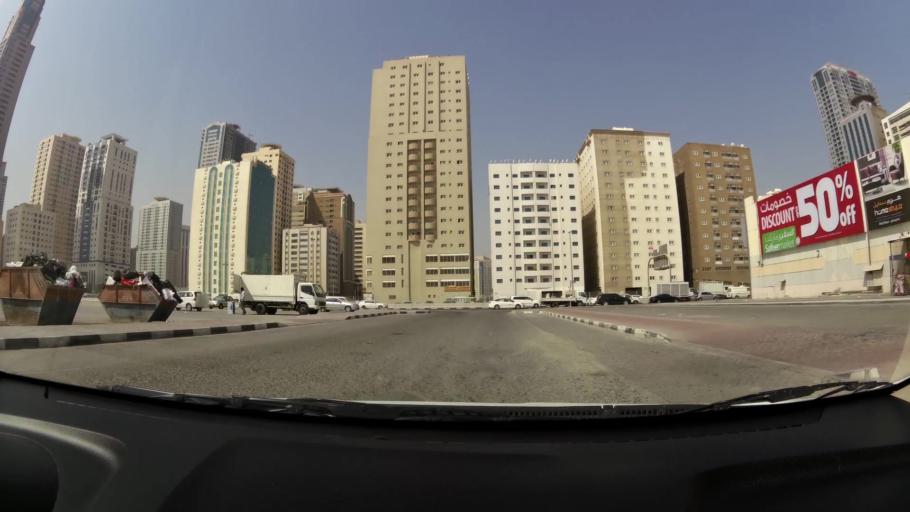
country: AE
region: Ash Shariqah
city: Sharjah
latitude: 25.3079
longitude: 55.3810
